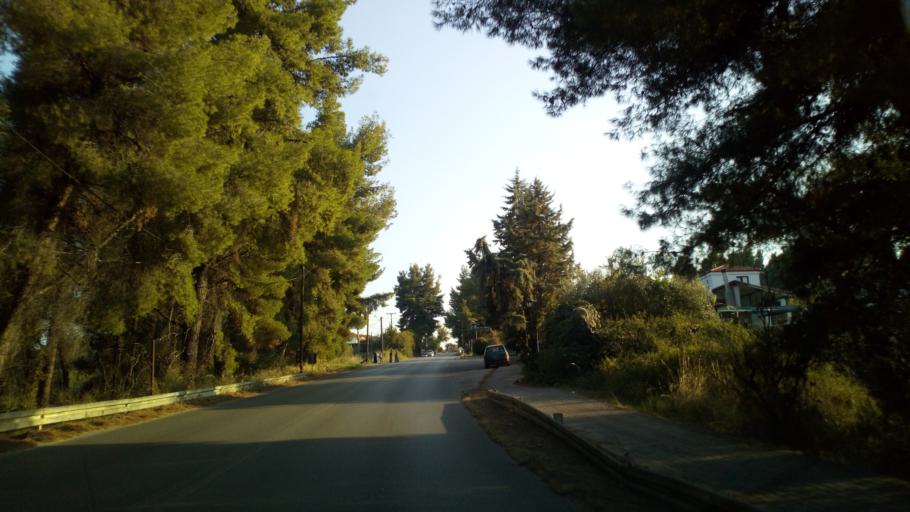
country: GR
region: Central Macedonia
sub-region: Nomos Chalkidikis
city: Pefkochori
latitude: 39.9470
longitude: 23.6741
